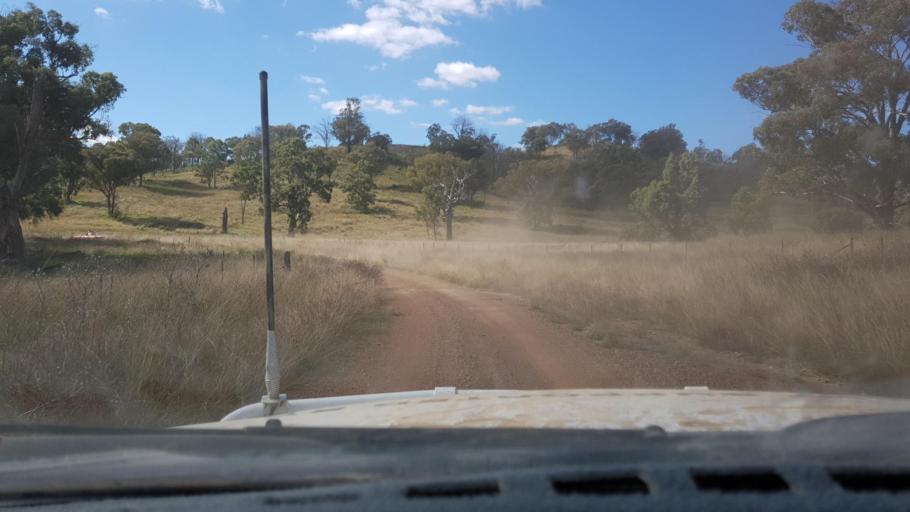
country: AU
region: New South Wales
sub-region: Tamworth Municipality
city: Manilla
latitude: -30.4412
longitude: 150.8368
